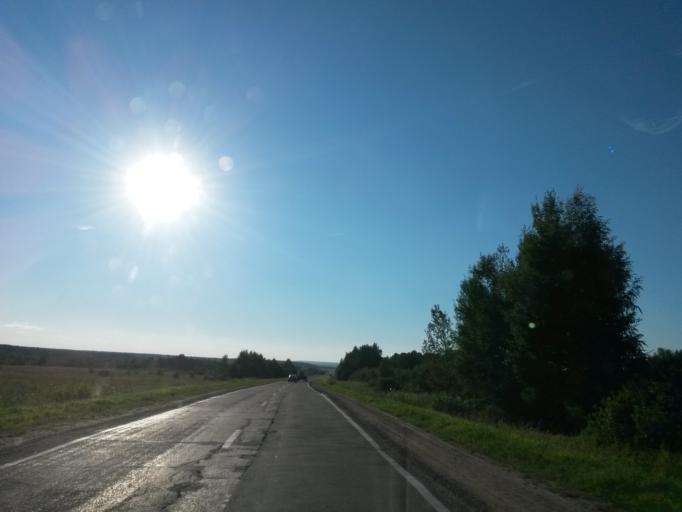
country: RU
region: Jaroslavl
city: Gavrilov-Yam
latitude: 57.2745
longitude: 39.9386
